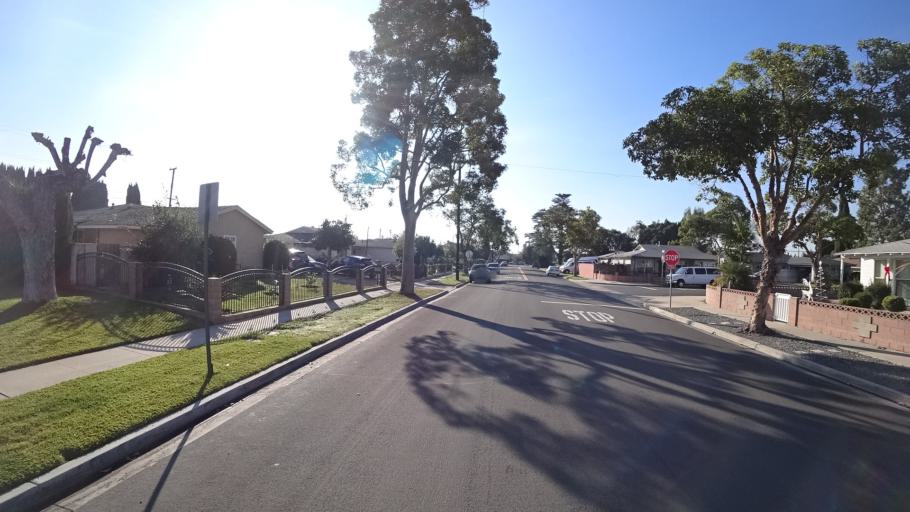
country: US
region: California
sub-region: Orange County
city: Santa Ana
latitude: 33.7733
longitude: -117.8991
